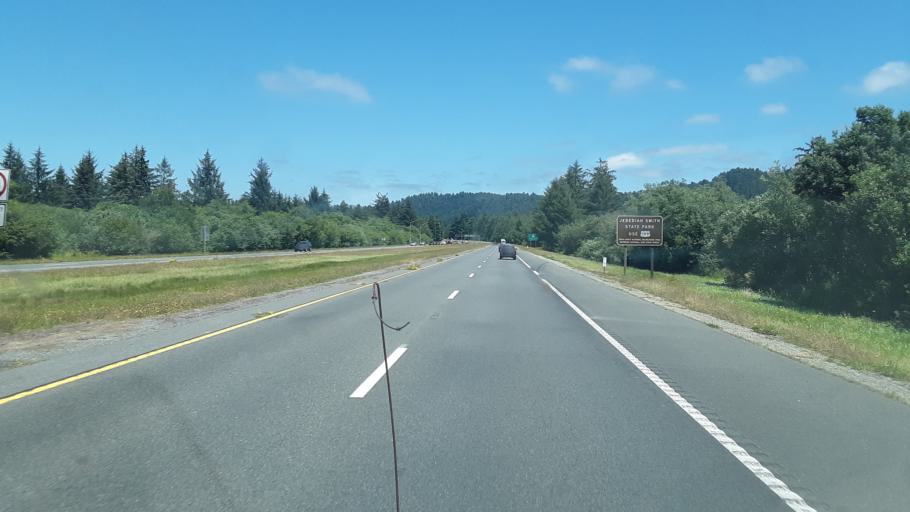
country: US
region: California
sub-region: Del Norte County
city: Bertsch-Oceanview
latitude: 41.7937
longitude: -124.1588
